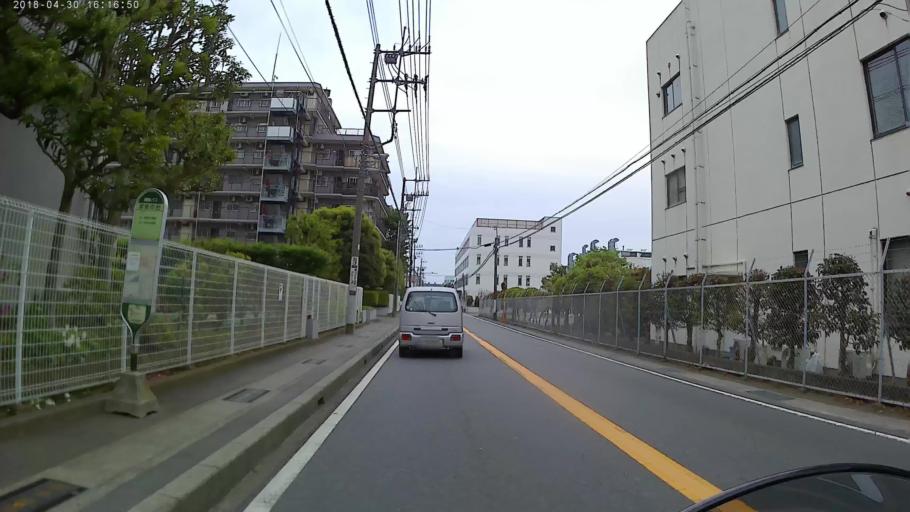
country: JP
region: Kanagawa
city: Minami-rinkan
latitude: 35.4824
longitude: 139.4317
